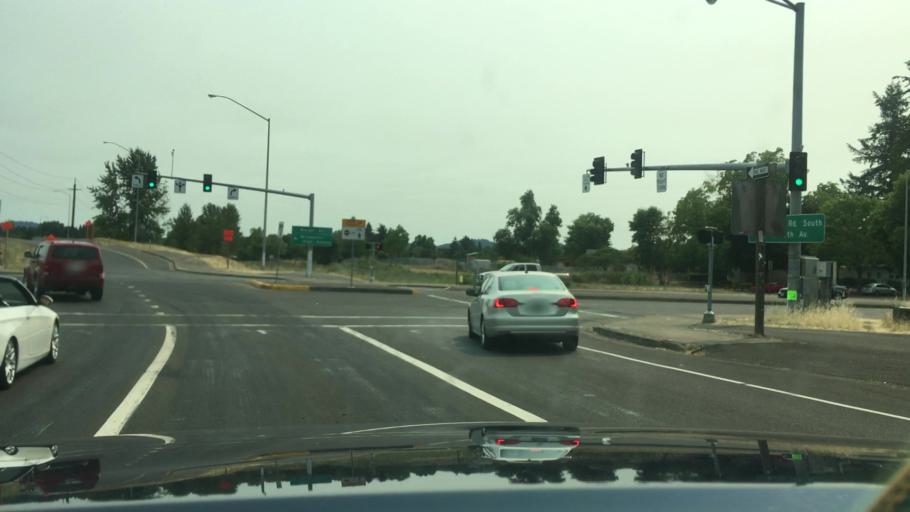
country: US
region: Oregon
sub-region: Lane County
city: Eugene
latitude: 44.0849
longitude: -123.1731
